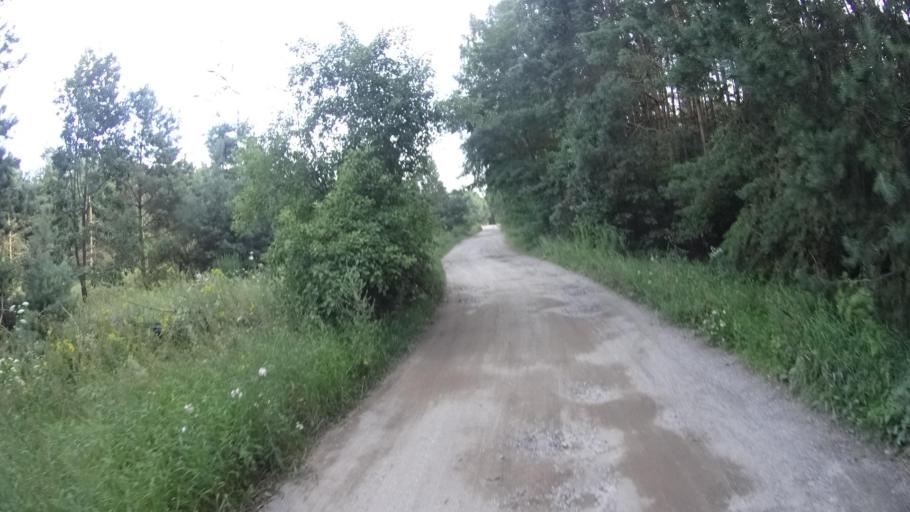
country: PL
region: Masovian Voivodeship
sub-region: Powiat piaseczynski
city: Tarczyn
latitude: 51.9699
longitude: 20.8540
